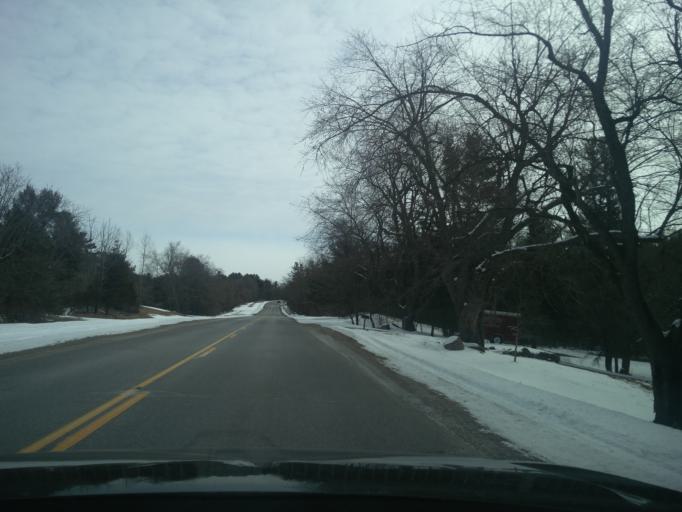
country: US
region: New York
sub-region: Jefferson County
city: Alexandria Bay
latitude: 44.3682
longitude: -75.9951
